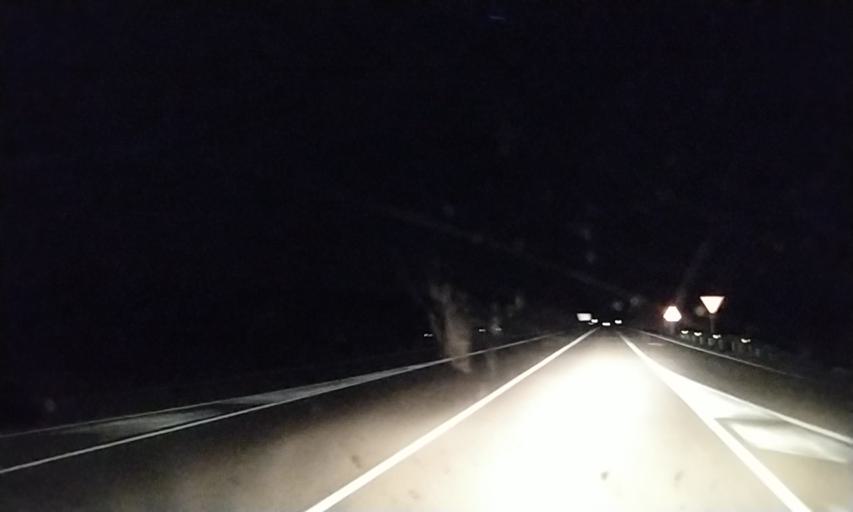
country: ES
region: Castille and Leon
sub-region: Provincia de Salamanca
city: Herguijuela de Ciudad Rodrigo
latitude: 40.4819
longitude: -6.5788
